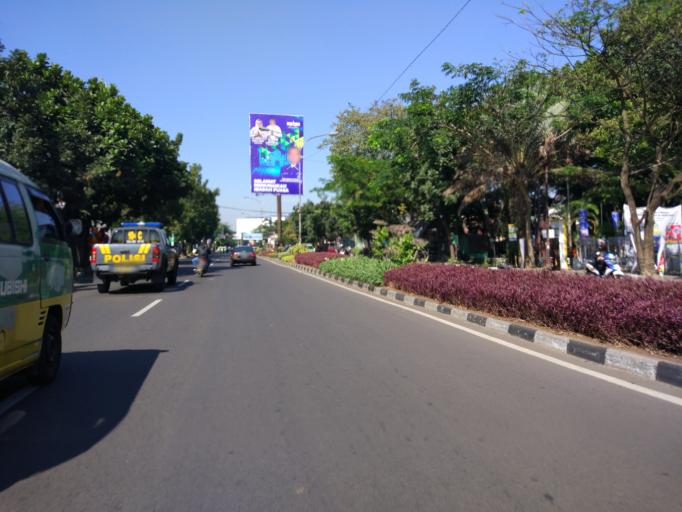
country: ID
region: West Java
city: Bandung
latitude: -6.9305
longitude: 107.6263
